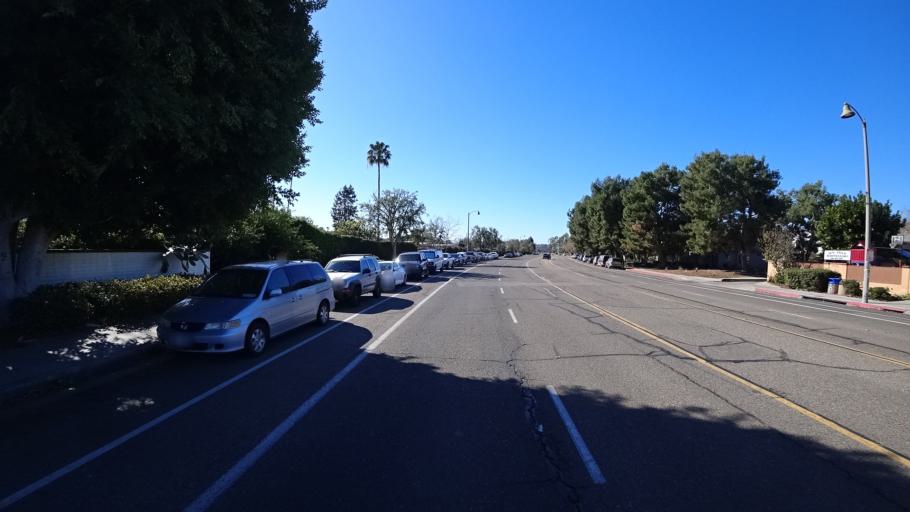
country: US
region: California
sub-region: Orange County
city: San Juan Capistrano
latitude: 33.4953
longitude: -117.6679
